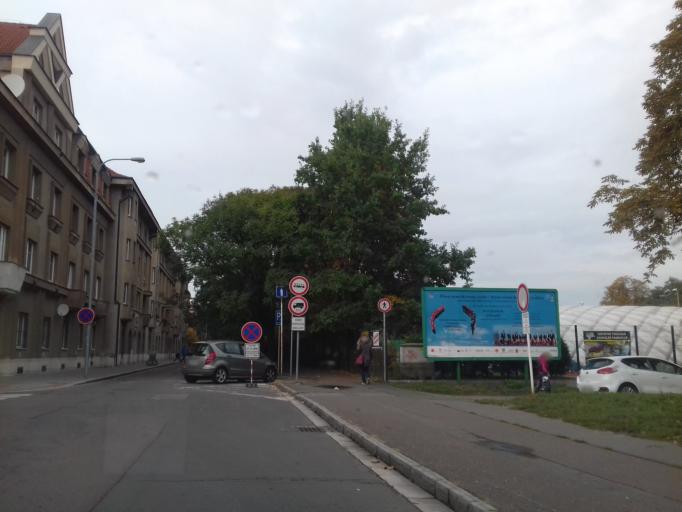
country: CZ
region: Pardubicky
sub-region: Okres Pardubice
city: Pardubice
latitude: 50.0357
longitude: 15.7811
